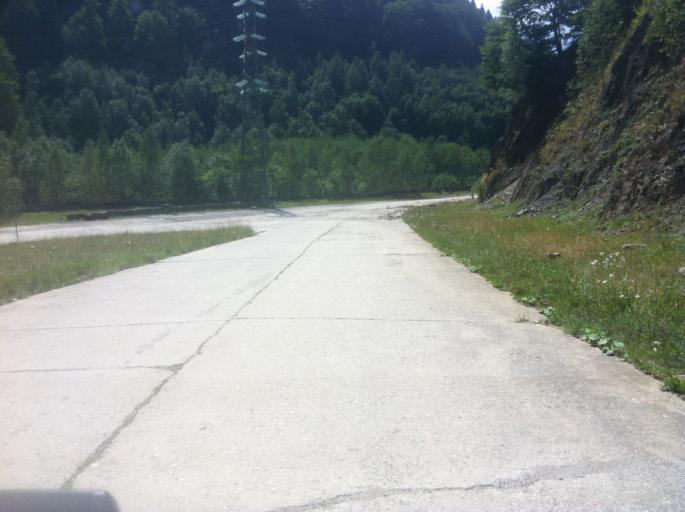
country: RO
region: Hunedoara
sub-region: Comuna Rau de Mori
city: Brazi
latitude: 45.3455
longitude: 22.7353
